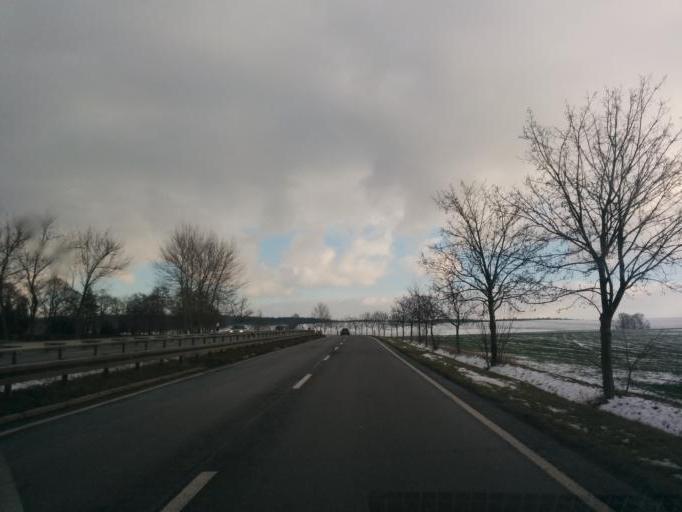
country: DE
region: Saxony
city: Niederwiesa
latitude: 50.8605
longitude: 13.0175
